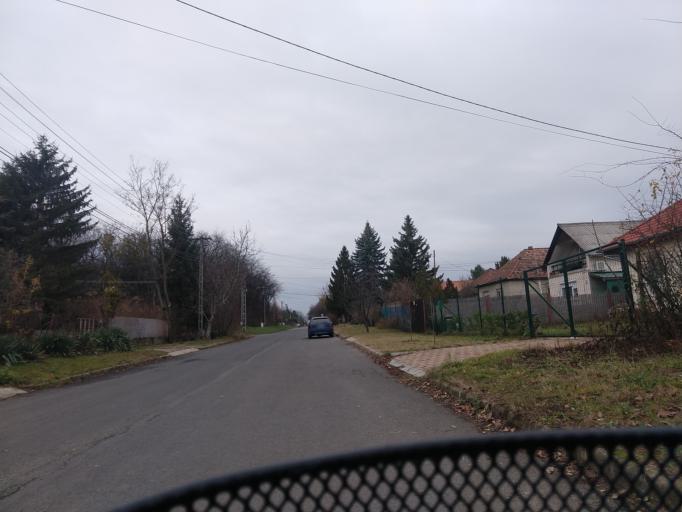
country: HU
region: Pest
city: Erdokertes
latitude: 47.6700
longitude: 19.2902
